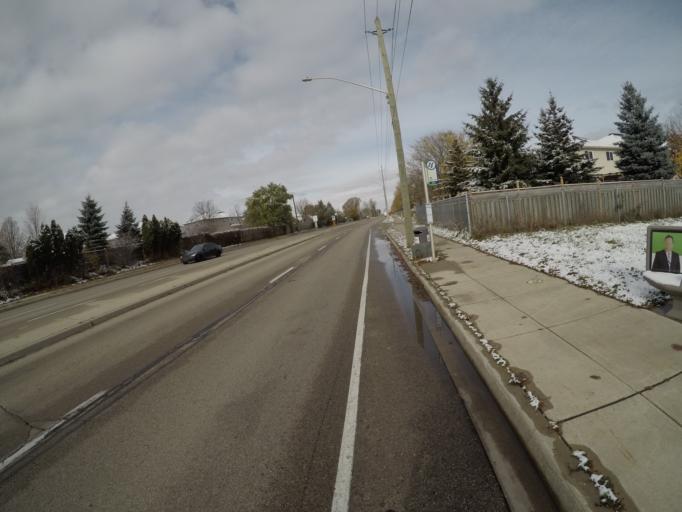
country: CA
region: Ontario
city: Waterloo
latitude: 43.4980
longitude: -80.4919
